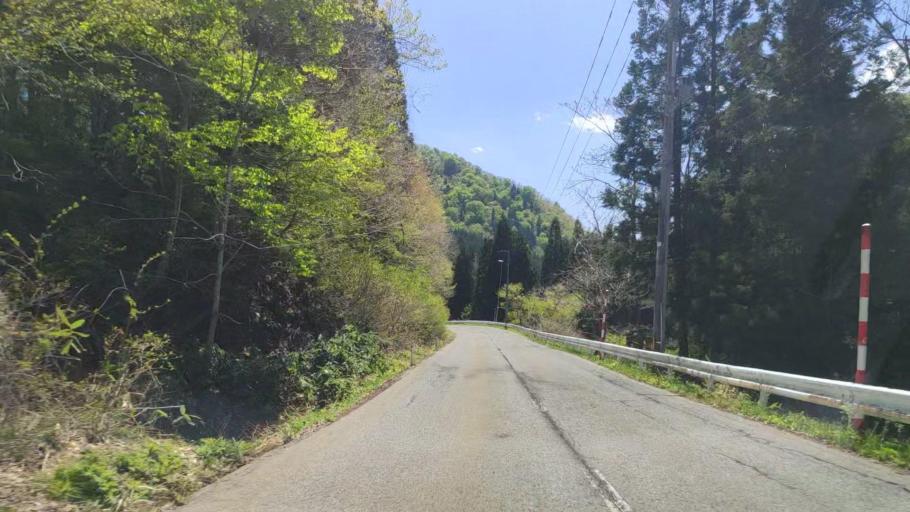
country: JP
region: Yamagata
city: Shinjo
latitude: 38.9563
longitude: 140.3580
